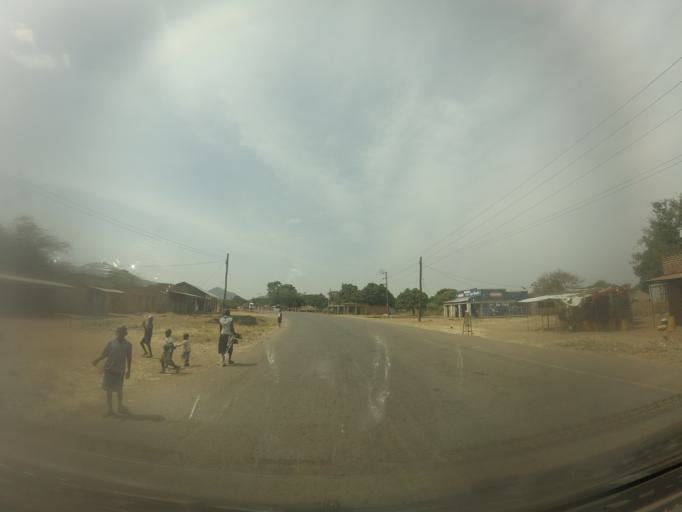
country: UG
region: Northern Region
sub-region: Arua District
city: Arua
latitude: 2.7749
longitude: 31.0365
